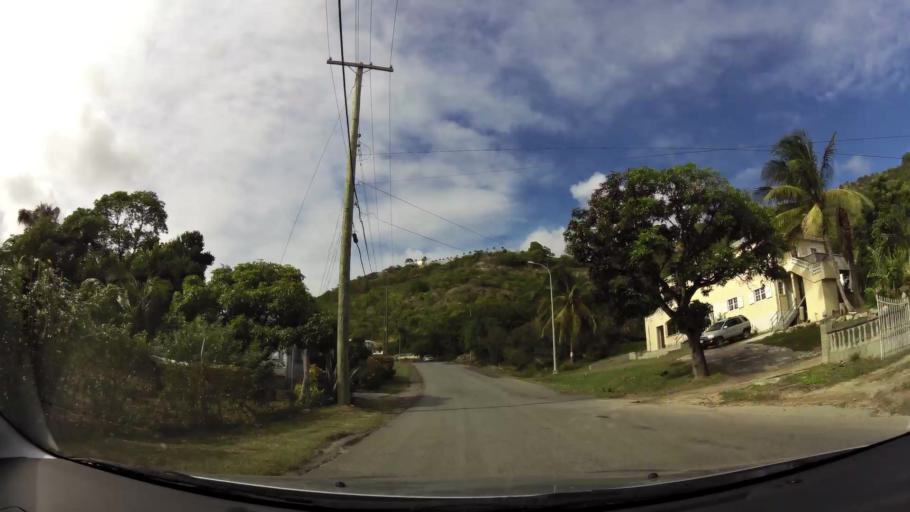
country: AG
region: Saint Paul
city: Falmouth
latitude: 17.0272
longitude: -61.7813
